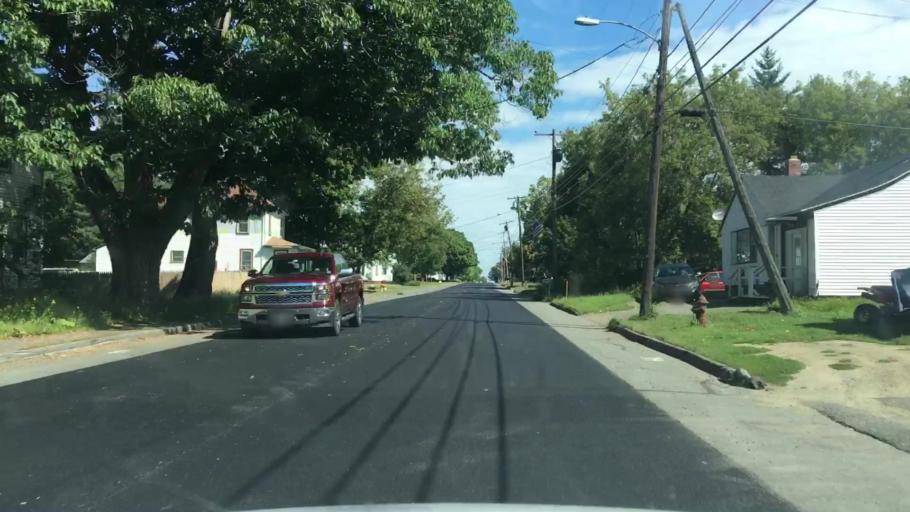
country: US
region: Maine
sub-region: Penobscot County
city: Corinna
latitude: 44.9234
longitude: -69.2584
